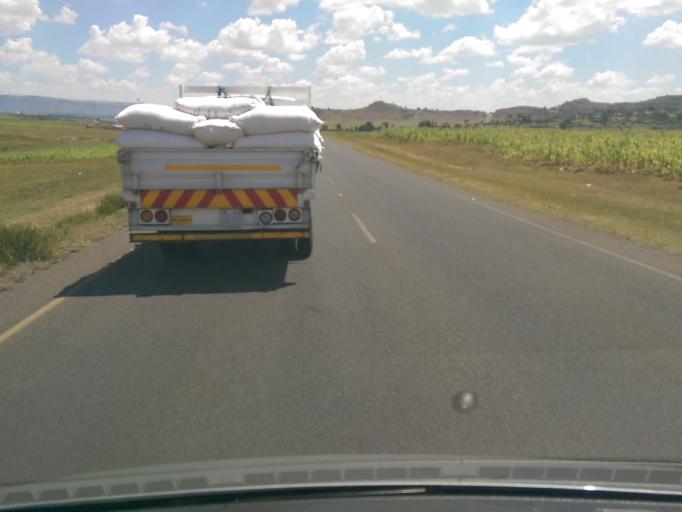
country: LS
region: Maseru
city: Maseru
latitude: -29.4199
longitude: 27.6573
